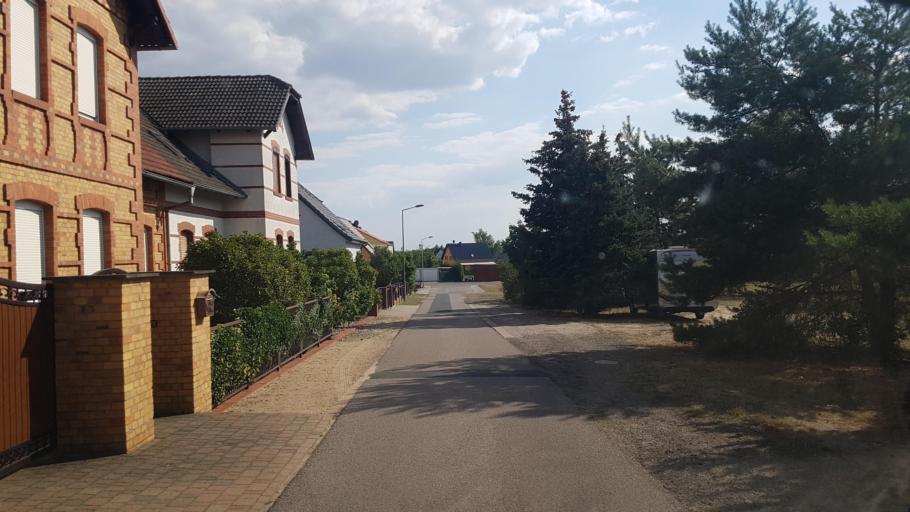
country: DE
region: Saxony-Anhalt
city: Jessen
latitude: 51.7949
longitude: 12.9713
